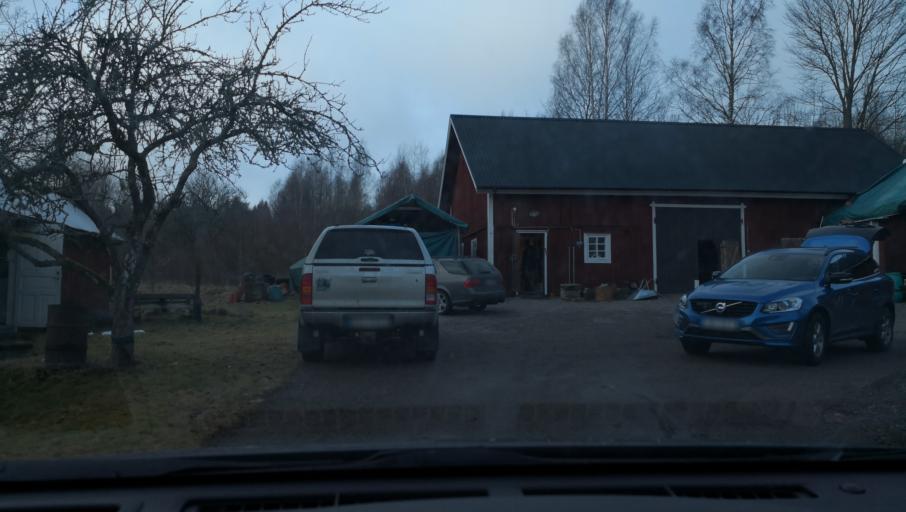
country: SE
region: Vaestra Goetaland
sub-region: Gullspangs Kommun
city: Gullspang
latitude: 58.9631
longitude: 14.0935
